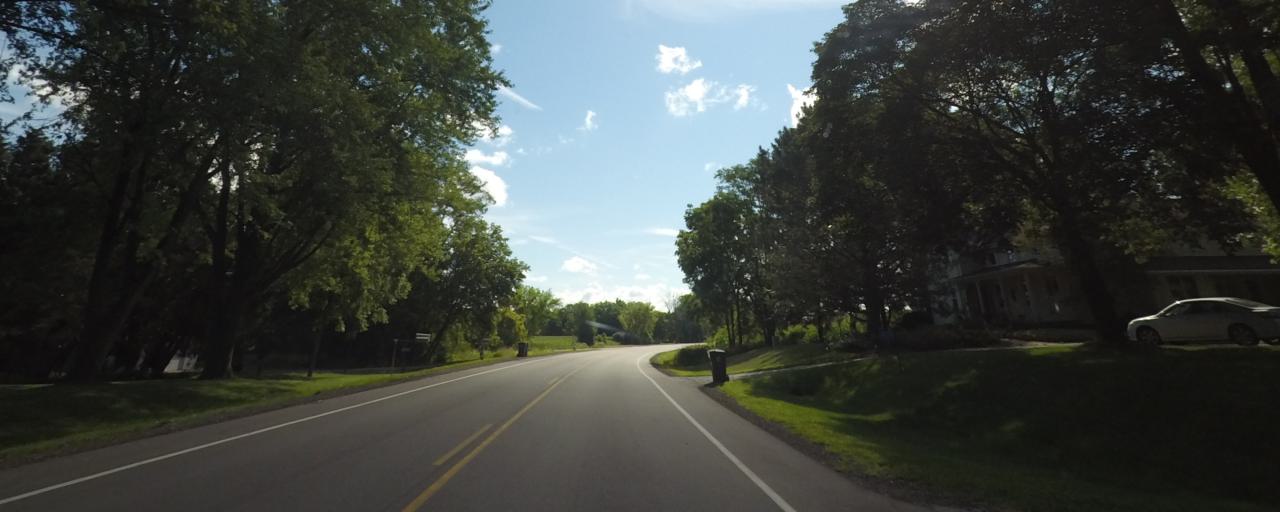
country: US
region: Wisconsin
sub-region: Waukesha County
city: Oconomowoc
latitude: 43.0761
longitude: -88.5619
